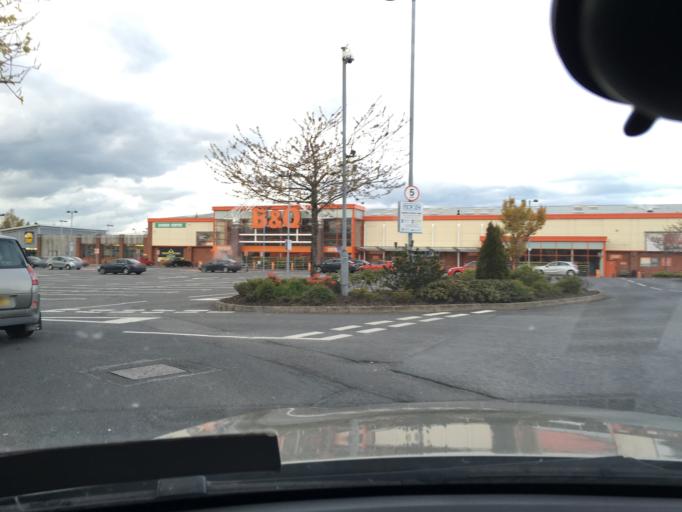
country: GB
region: Northern Ireland
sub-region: Newry and Mourne District
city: Newry
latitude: 54.1914
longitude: -6.3500
